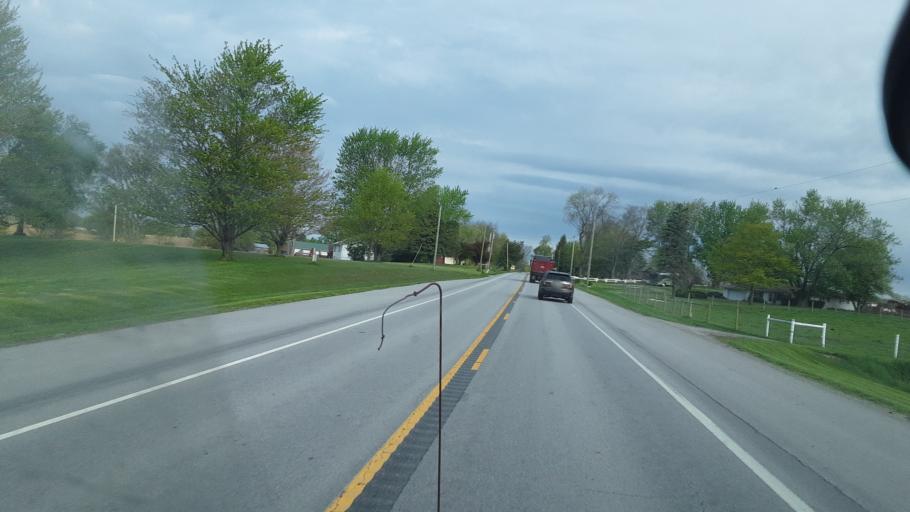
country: US
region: Indiana
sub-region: Whitley County
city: Churubusco
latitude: 41.2503
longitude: -85.3407
